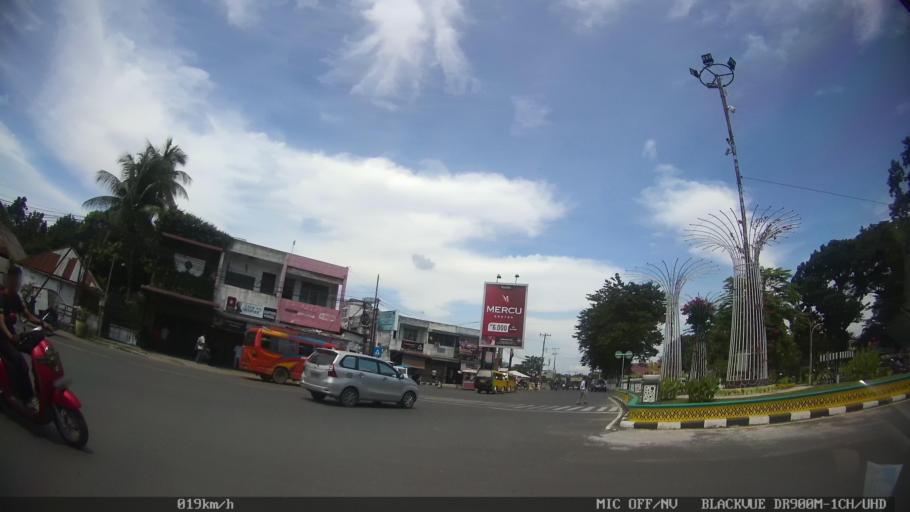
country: ID
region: North Sumatra
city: Binjai
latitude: 3.6018
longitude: 98.4807
